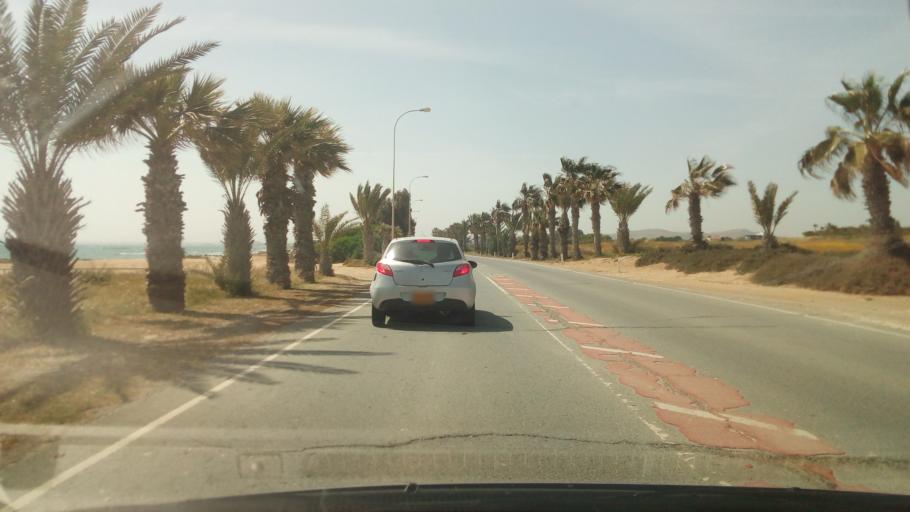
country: CY
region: Larnaka
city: Pyla
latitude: 34.9802
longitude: 33.7071
